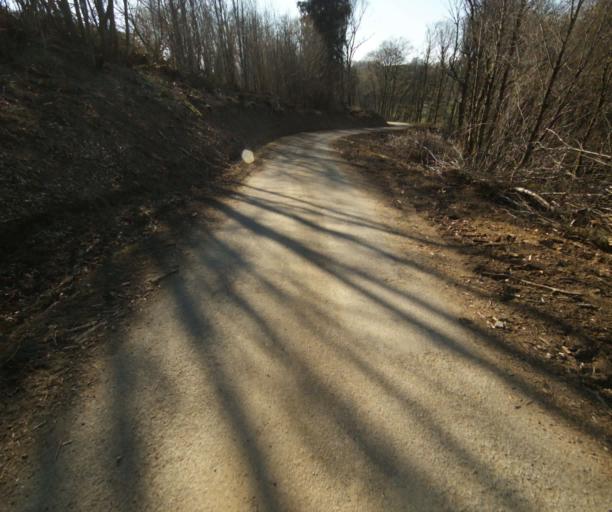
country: FR
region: Limousin
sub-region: Departement de la Correze
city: Chamboulive
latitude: 45.4869
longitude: 1.6924
